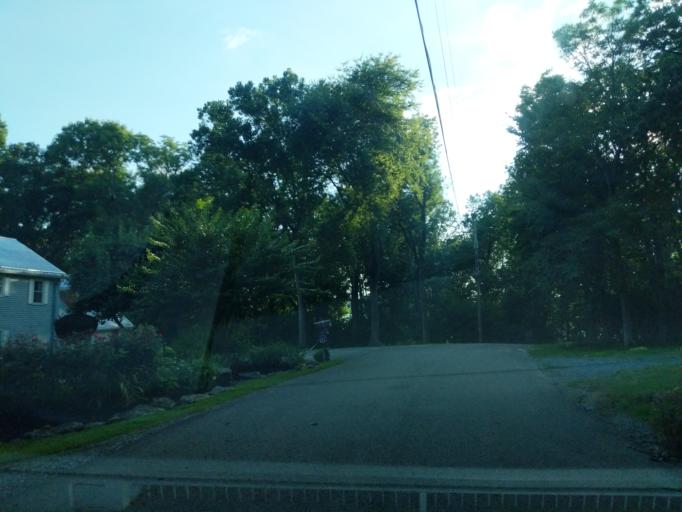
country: US
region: Tennessee
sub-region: Sumner County
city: Hendersonville
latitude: 36.2956
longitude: -86.6463
